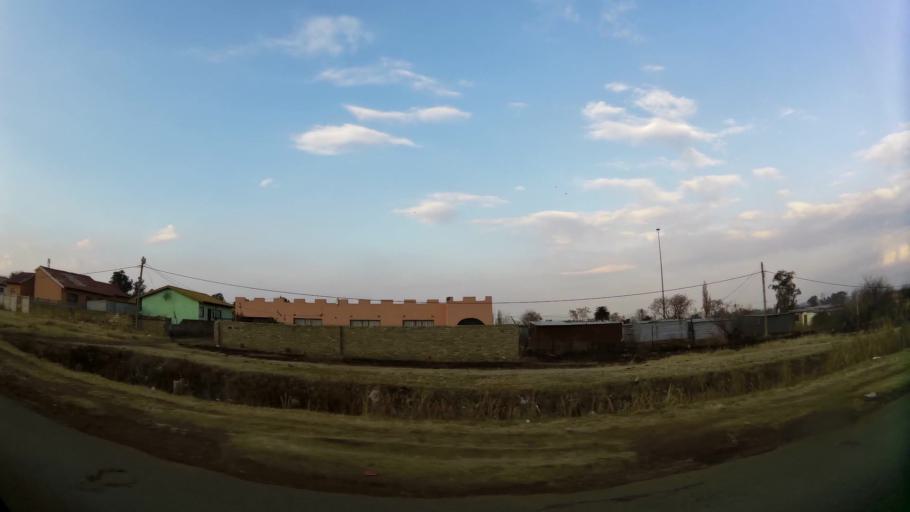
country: ZA
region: Gauteng
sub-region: City of Johannesburg Metropolitan Municipality
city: Orange Farm
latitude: -26.5405
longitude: 27.8326
